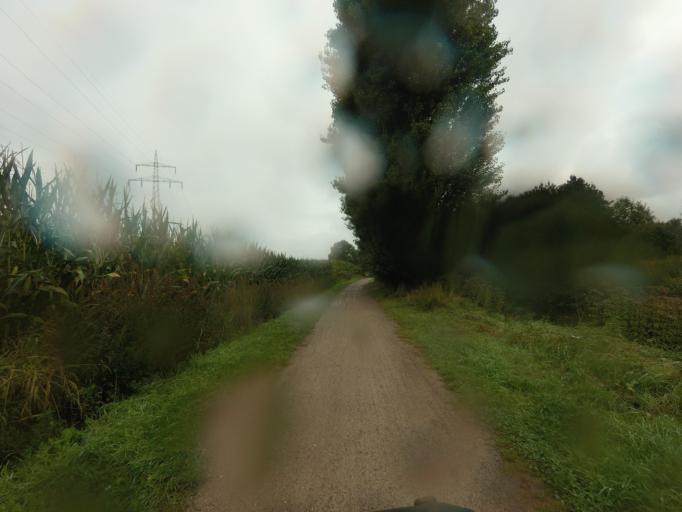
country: DE
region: North Rhine-Westphalia
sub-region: Regierungsbezirk Munster
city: Gronau
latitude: 52.1923
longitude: 7.0168
